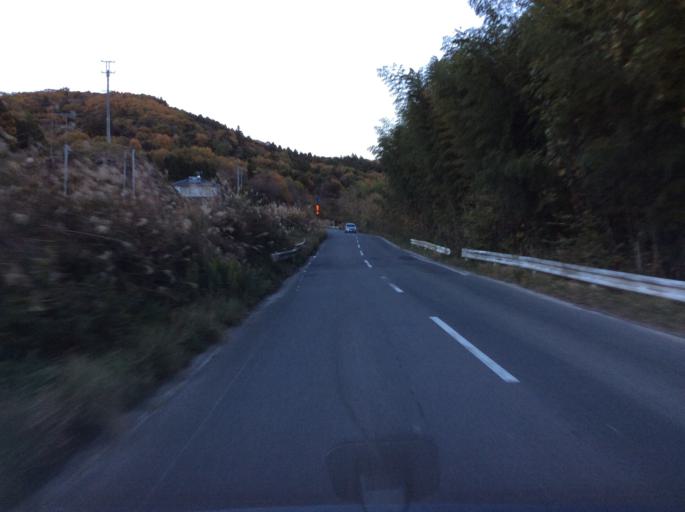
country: JP
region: Fukushima
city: Iwaki
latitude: 37.0971
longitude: 140.8598
